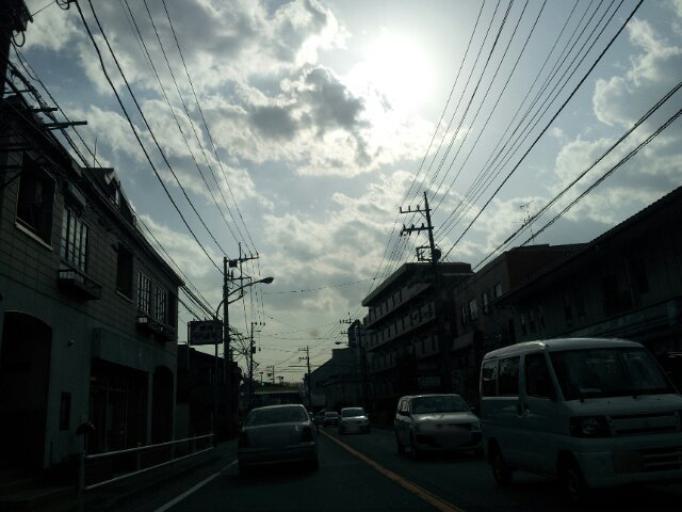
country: JP
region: Kanagawa
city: Yokohama
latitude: 35.4197
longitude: 139.5507
